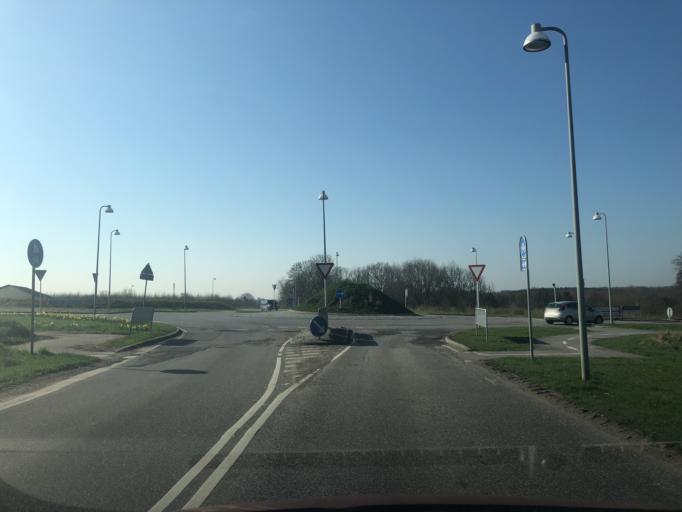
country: DK
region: Zealand
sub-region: Faxe Kommune
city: Fakse
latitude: 55.2562
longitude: 12.0985
